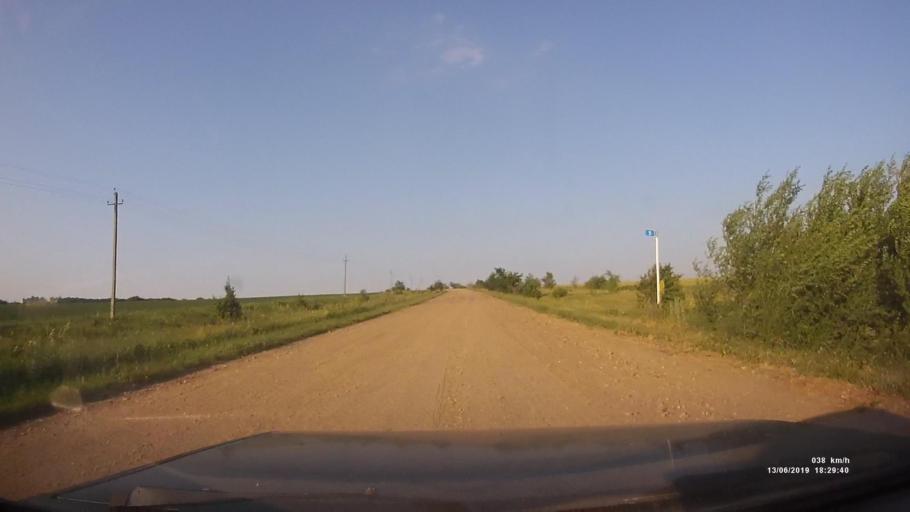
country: RU
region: Rostov
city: Kazanskaya
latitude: 49.8595
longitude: 41.3429
